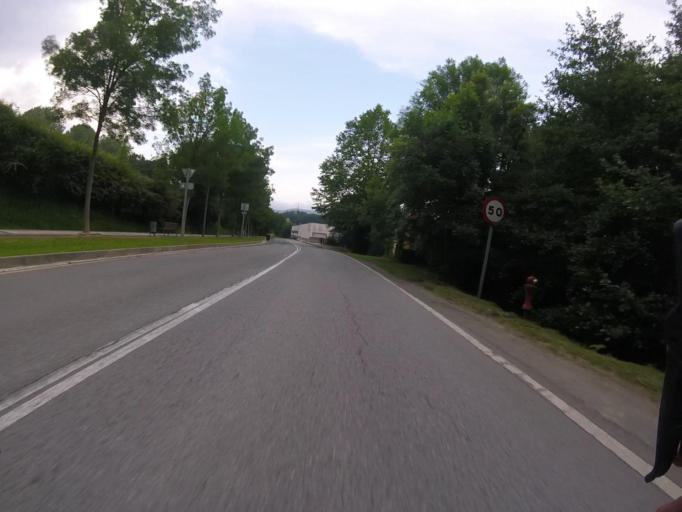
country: ES
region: Basque Country
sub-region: Provincia de Guipuzcoa
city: Errenteria
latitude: 43.3029
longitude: -1.9045
